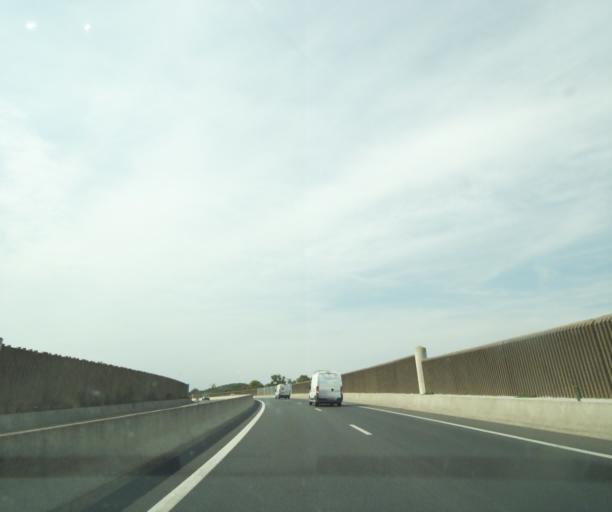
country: FR
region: Centre
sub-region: Departement d'Indre-et-Loire
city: Saint-Cyr-sur-Loire
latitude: 47.3988
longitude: 0.6478
